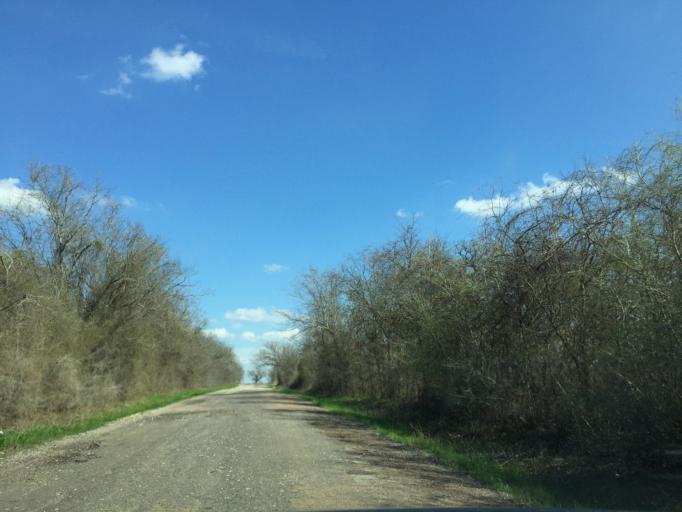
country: US
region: Texas
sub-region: Milam County
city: Thorndale
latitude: 30.5853
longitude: -97.1867
